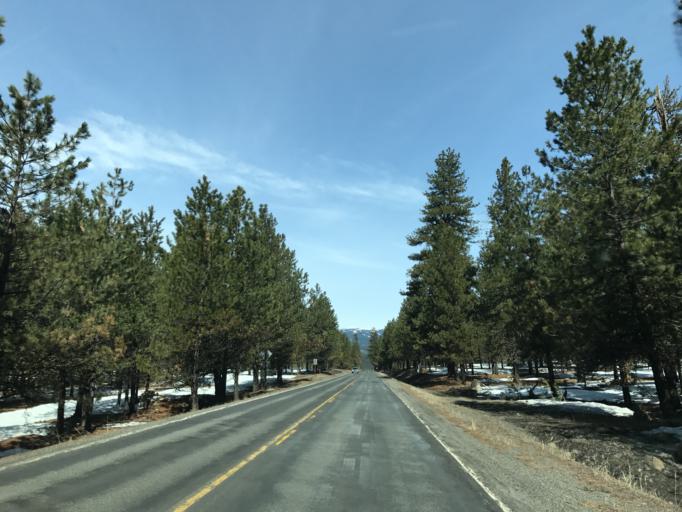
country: US
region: Idaho
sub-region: Valley County
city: McCall
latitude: 44.9362
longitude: -116.1657
